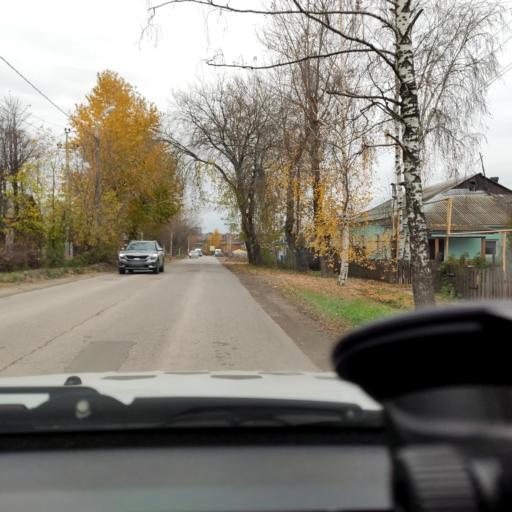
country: RU
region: Perm
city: Perm
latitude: 57.9944
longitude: 56.3102
